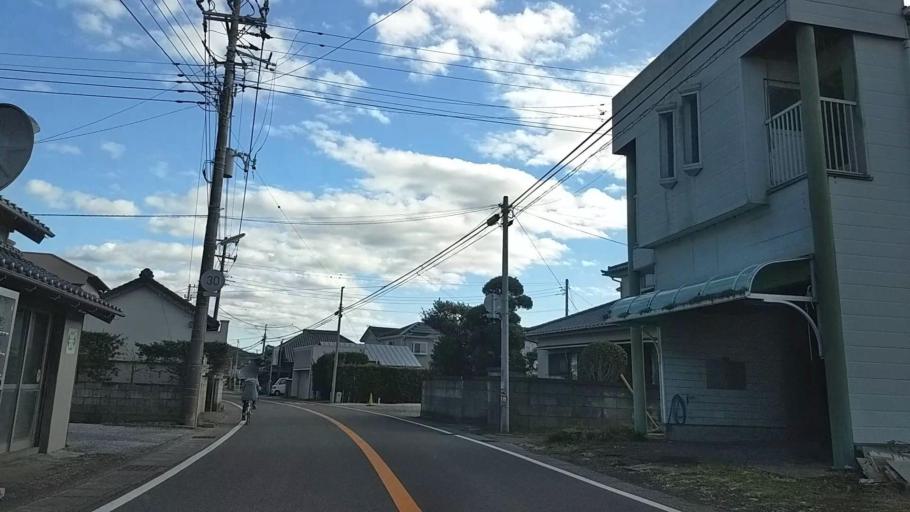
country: JP
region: Chiba
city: Tateyama
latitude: 35.0239
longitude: 139.8614
